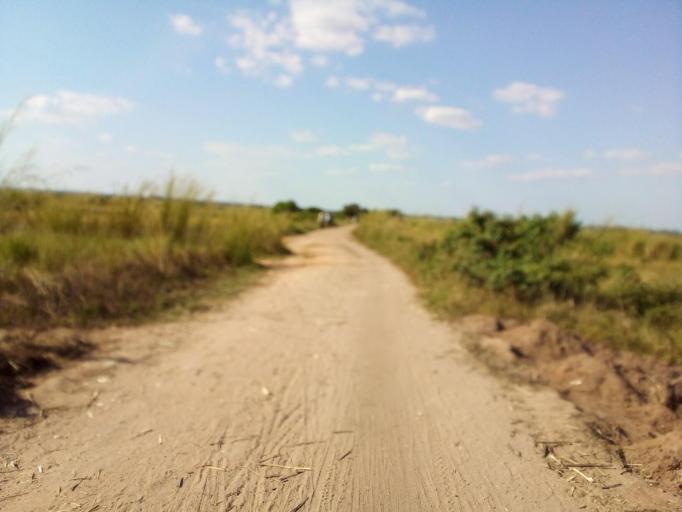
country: MZ
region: Zambezia
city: Quelimane
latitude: -17.5902
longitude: 36.8359
